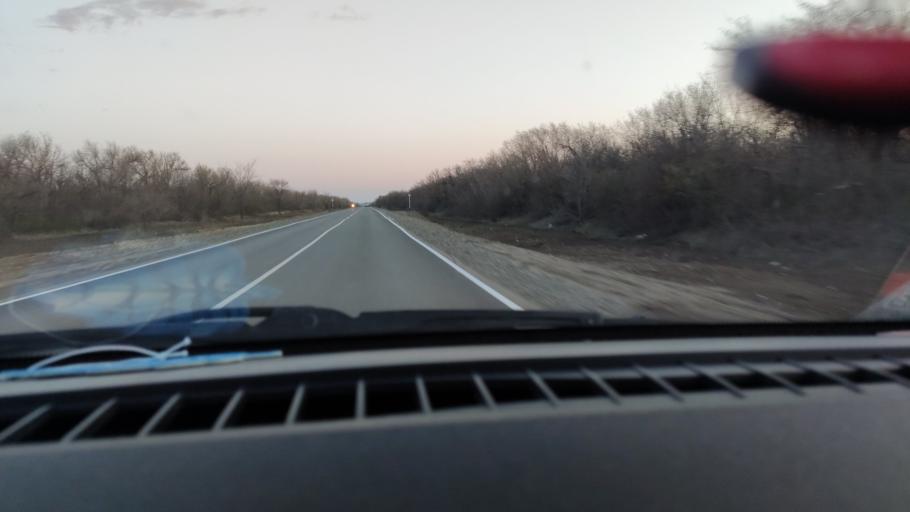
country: RU
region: Saratov
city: Privolzhskiy
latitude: 51.1448
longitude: 45.9614
